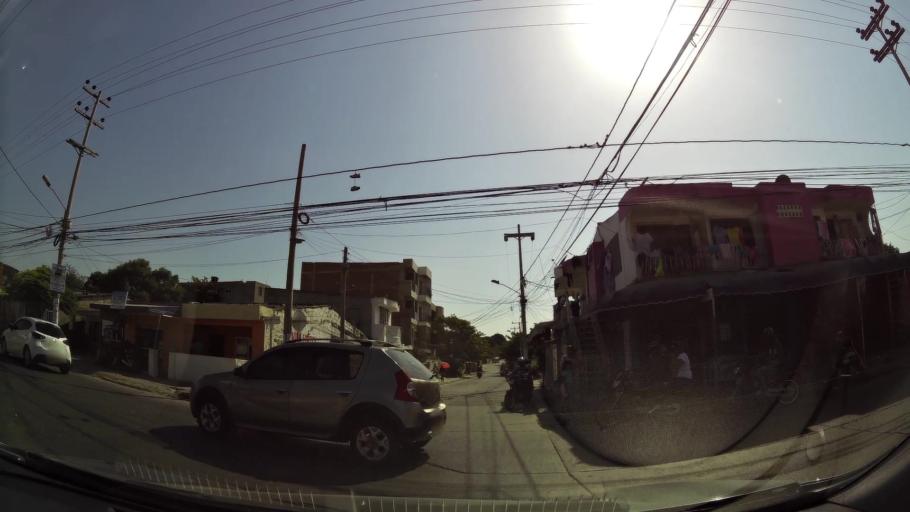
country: CO
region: Bolivar
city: Cartagena
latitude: 10.3996
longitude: -75.5000
